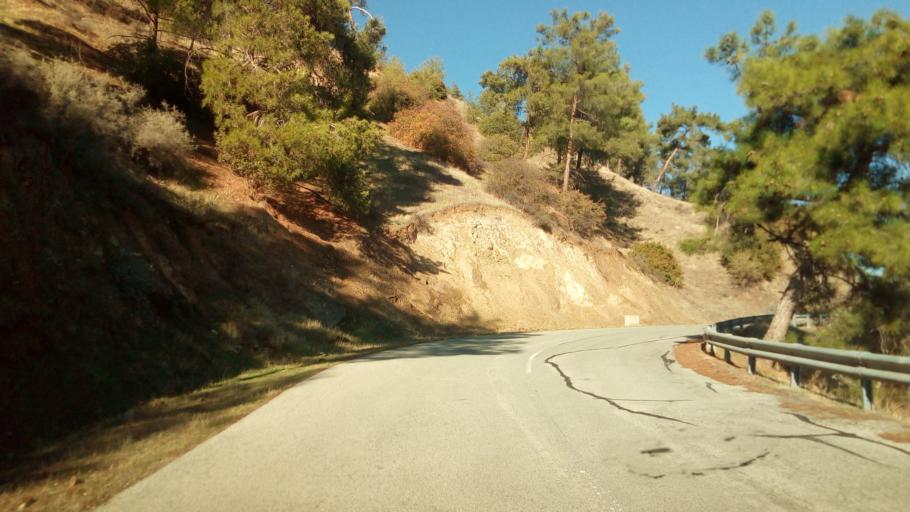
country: CY
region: Lefkosia
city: Lefka
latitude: 35.0920
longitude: 32.7922
